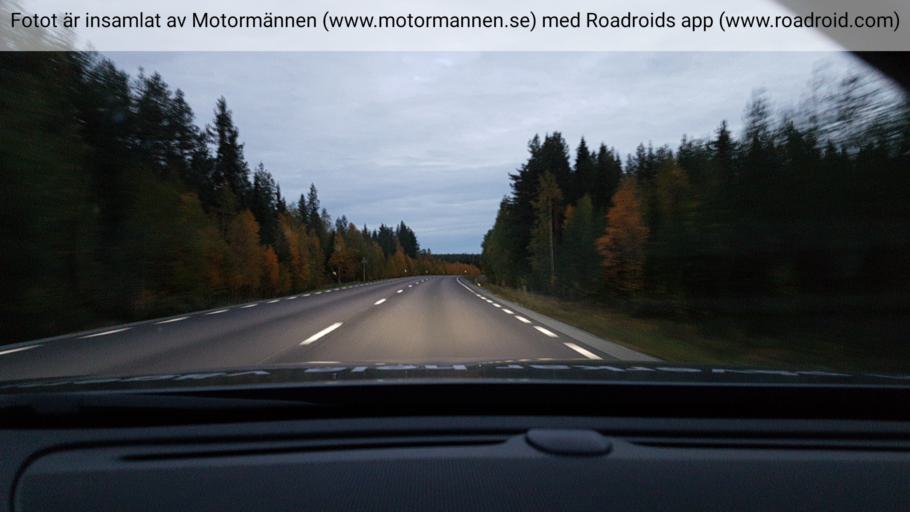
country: SE
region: Norrbotten
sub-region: Alvsbyns Kommun
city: AElvsbyn
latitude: 65.7302
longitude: 20.9828
